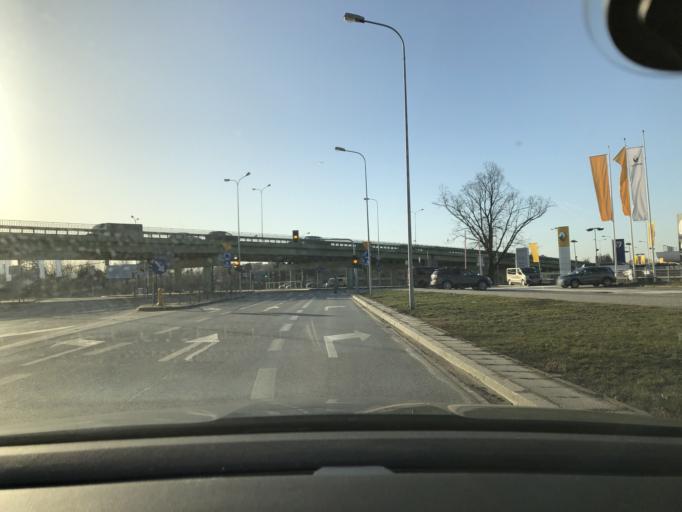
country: PL
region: Masovian Voivodeship
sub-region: Warszawa
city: Wlochy
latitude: 52.2107
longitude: 20.9490
